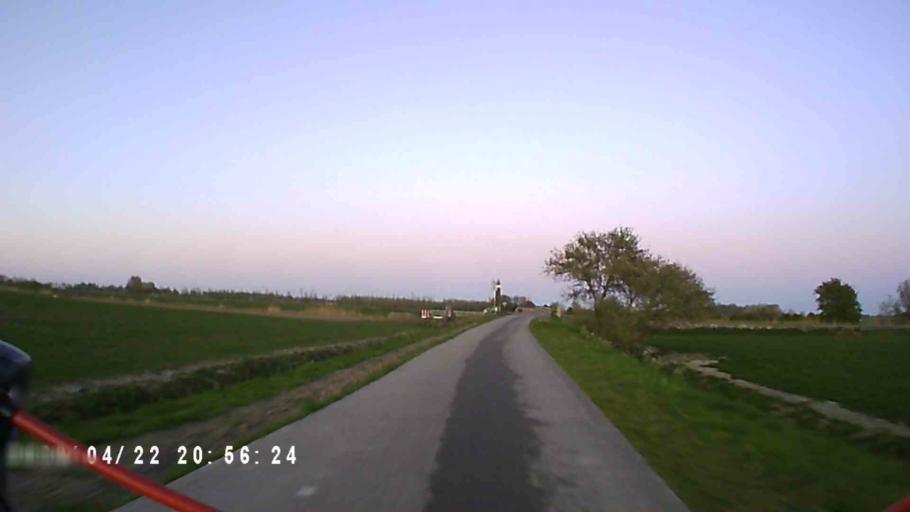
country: NL
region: Groningen
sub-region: Gemeente Winsum
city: Winsum
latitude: 53.3305
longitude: 6.5651
